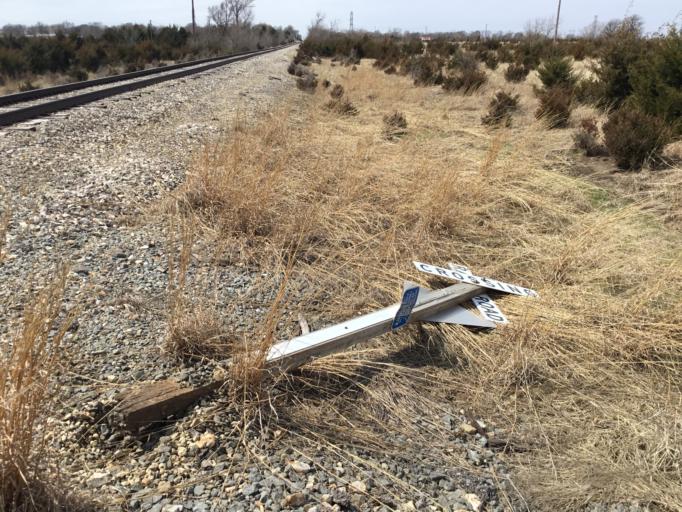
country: US
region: Kansas
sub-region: Butler County
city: El Dorado
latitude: 37.8227
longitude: -96.9172
